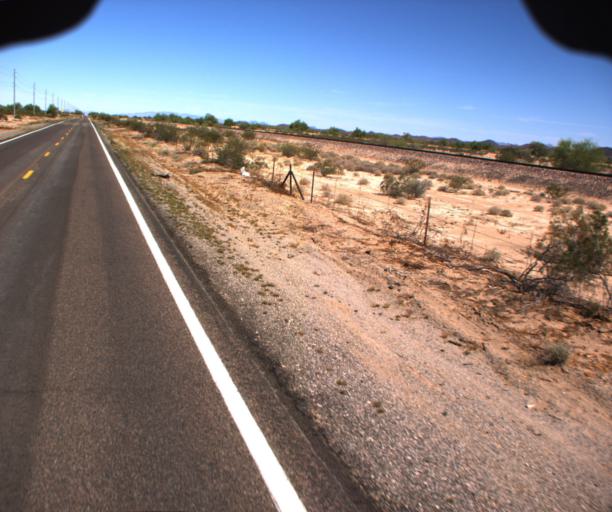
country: US
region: Arizona
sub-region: La Paz County
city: Salome
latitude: 33.8725
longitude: -113.9341
